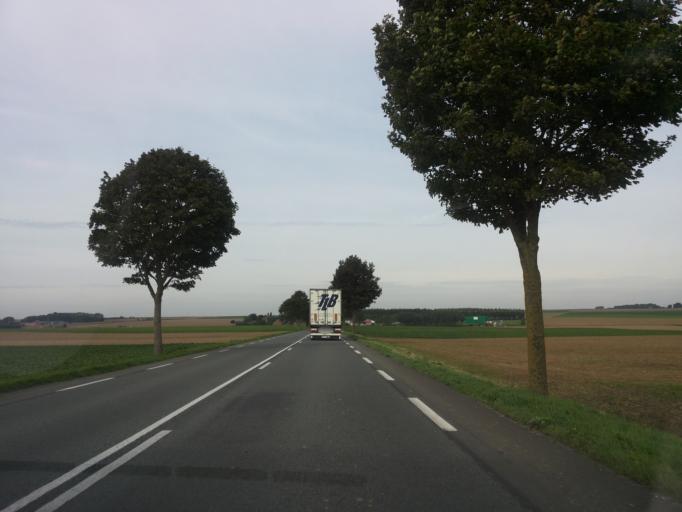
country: FR
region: Nord-Pas-de-Calais
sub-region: Departement du Pas-de-Calais
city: Ecourt-Saint-Quentin
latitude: 50.2256
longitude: 3.0295
